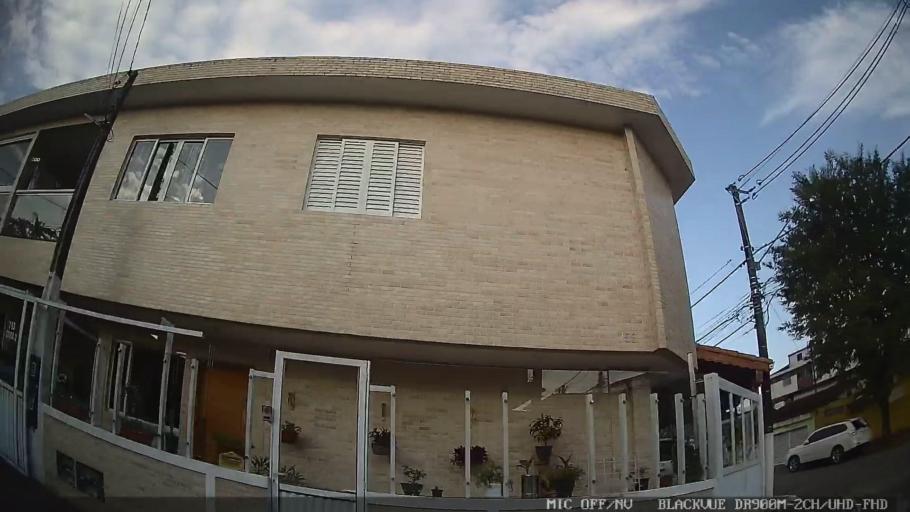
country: BR
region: Sao Paulo
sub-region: Cubatao
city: Cubatao
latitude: -23.8978
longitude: -46.4225
